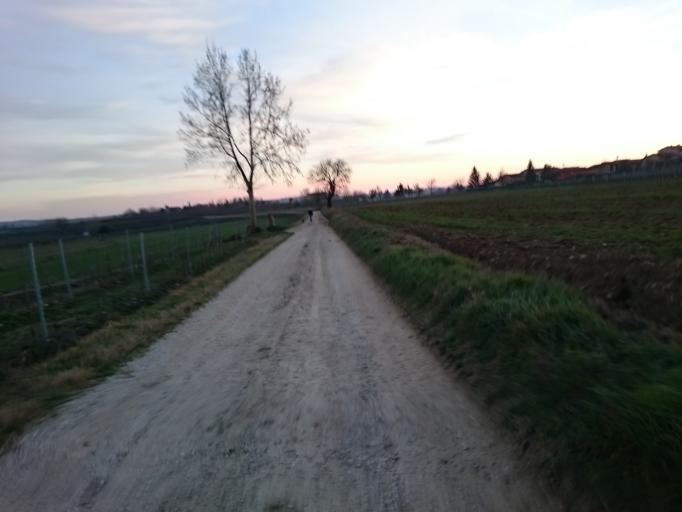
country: IT
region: Veneto
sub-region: Provincia di Verona
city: Castelnuovo del Garda
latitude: 45.4137
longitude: 10.7530
